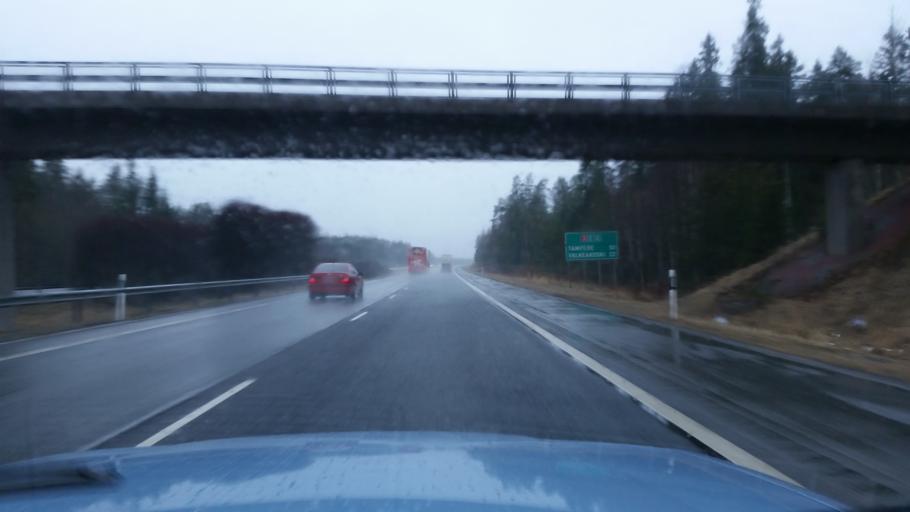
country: FI
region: Haeme
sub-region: Haemeenlinna
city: Kalvola
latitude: 61.1044
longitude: 24.1523
